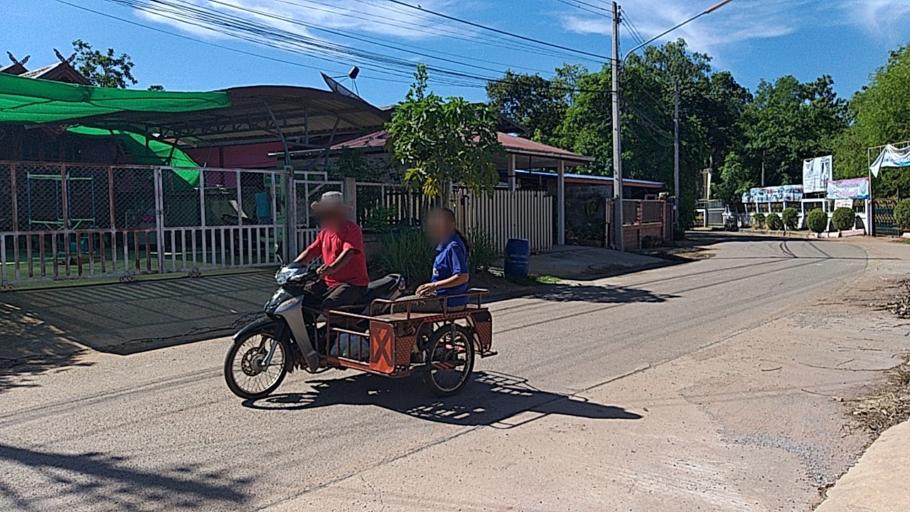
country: TH
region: Chaiyaphum
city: Ban Thaen
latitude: 16.4068
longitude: 102.3515
